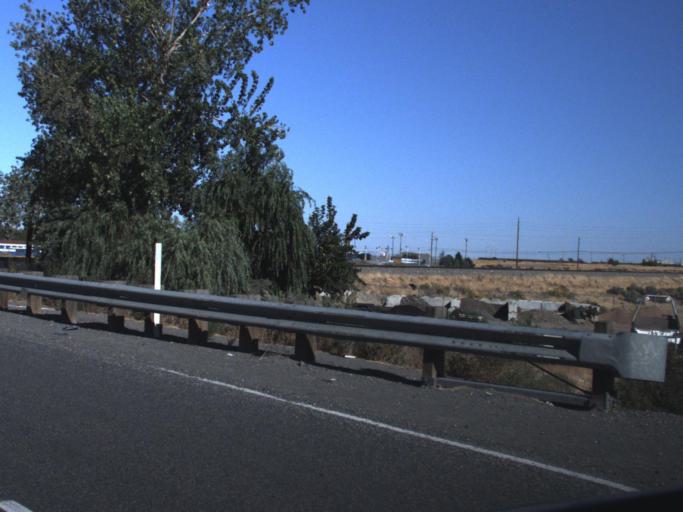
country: US
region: Washington
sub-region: Benton County
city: Richland
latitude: 46.3116
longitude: -119.2886
